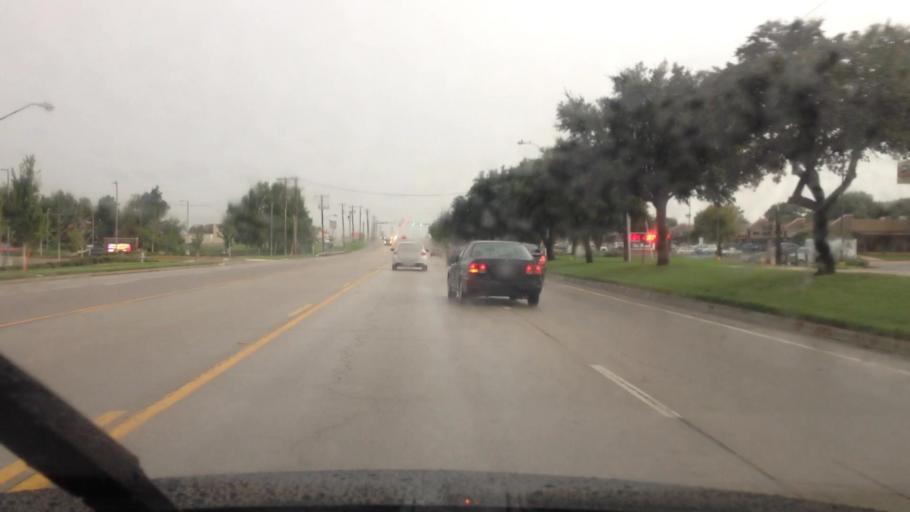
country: US
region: Texas
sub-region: Tarrant County
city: Colleyville
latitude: 32.8616
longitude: -97.1790
